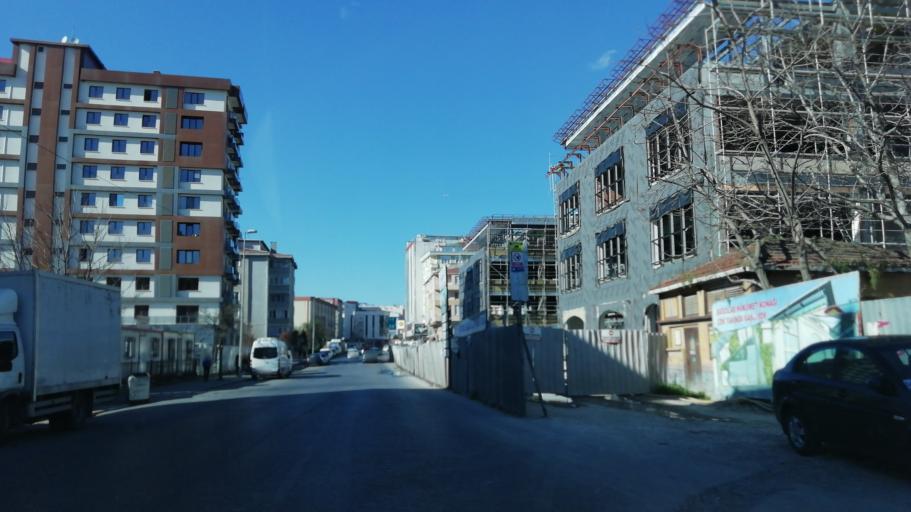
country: TR
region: Istanbul
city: Bagcilar
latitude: 41.0349
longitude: 28.8527
